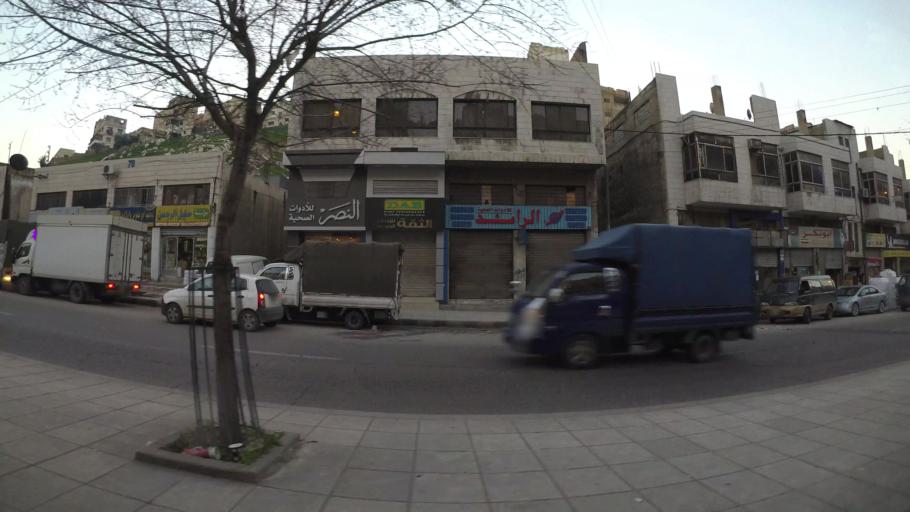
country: JO
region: Amman
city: Amman
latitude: 31.9384
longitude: 35.9238
